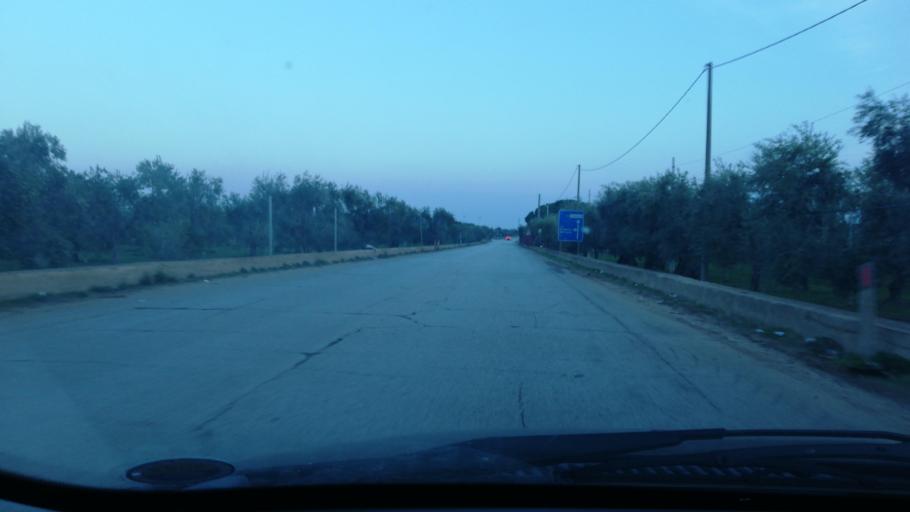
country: IT
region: Apulia
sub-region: Provincia di Bari
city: Bitonto
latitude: 41.1301
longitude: 16.7089
